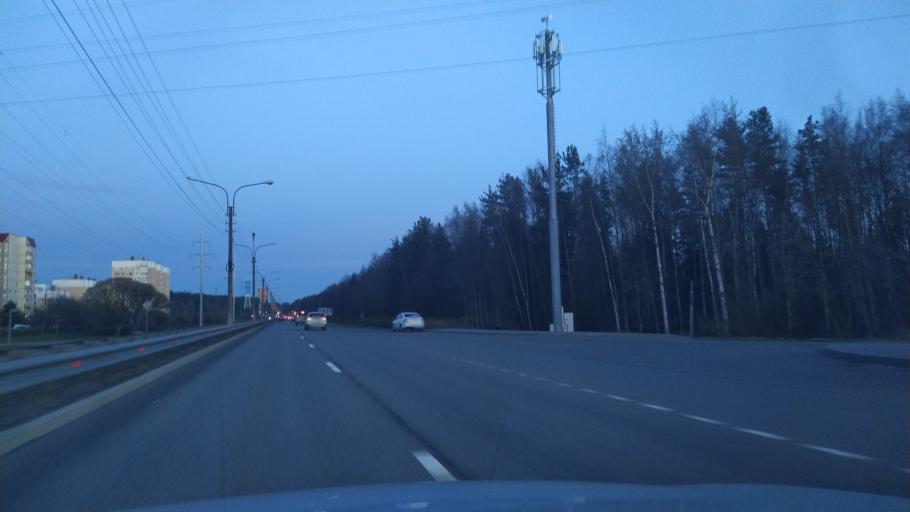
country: RU
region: St.-Petersburg
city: Razliv
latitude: 60.0800
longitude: 29.9605
